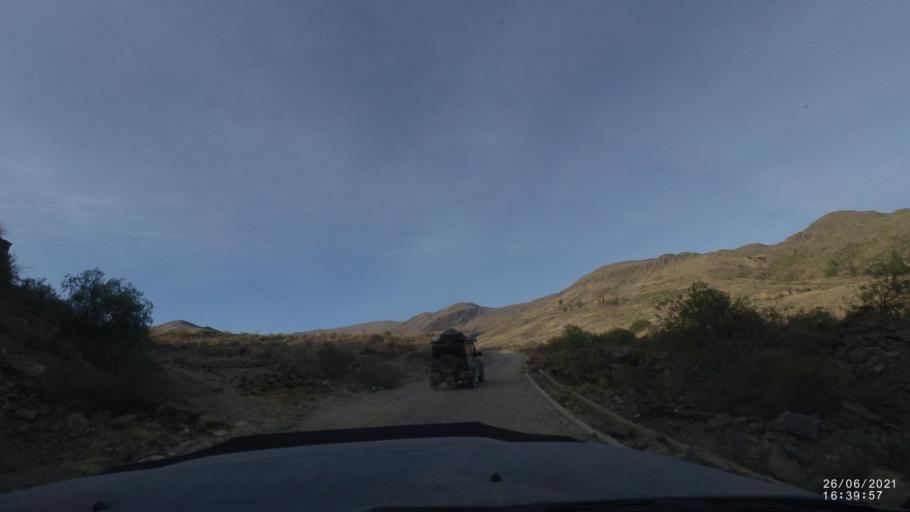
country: BO
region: Cochabamba
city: Arani
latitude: -17.7728
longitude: -65.8142
